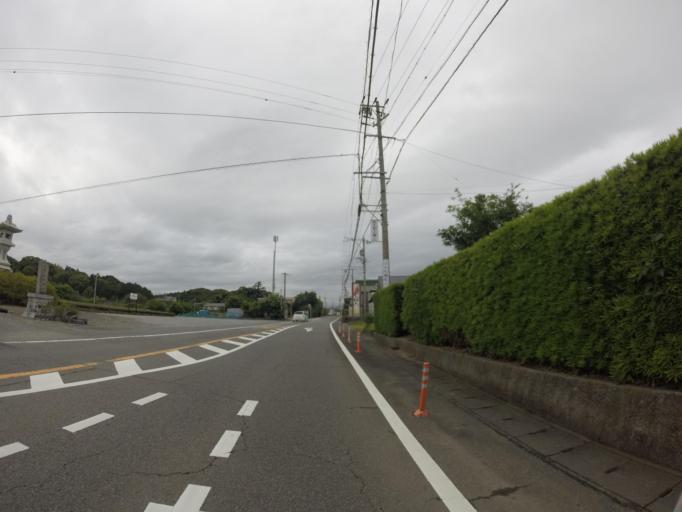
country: JP
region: Shizuoka
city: Sagara
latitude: 34.7298
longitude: 138.1619
